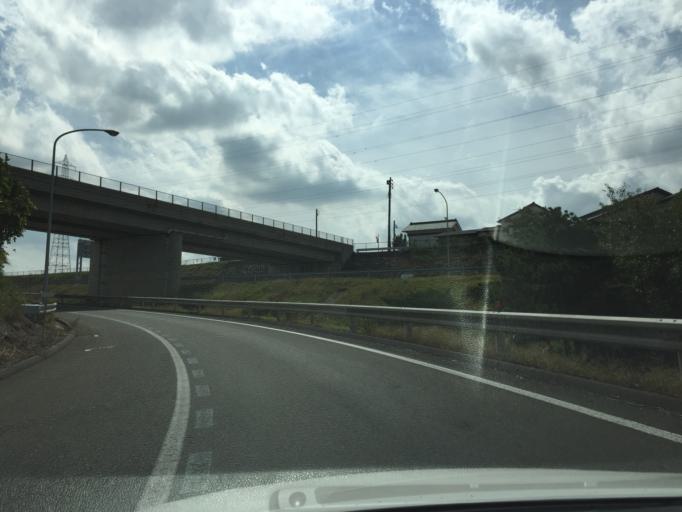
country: JP
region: Fukushima
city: Motomiya
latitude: 37.4654
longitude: 140.3554
